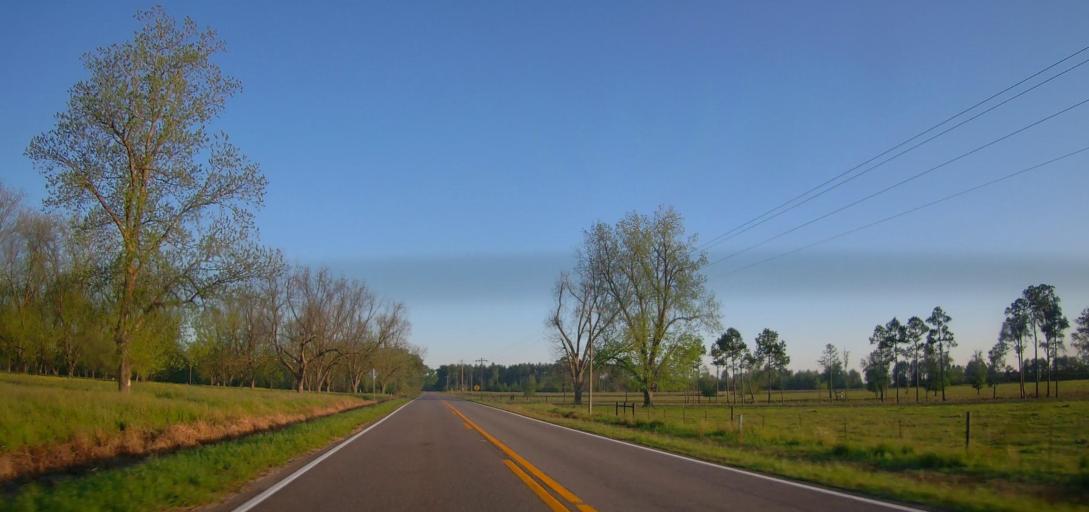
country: US
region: Georgia
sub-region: Irwin County
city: Ocilla
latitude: 31.6308
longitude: -83.2746
